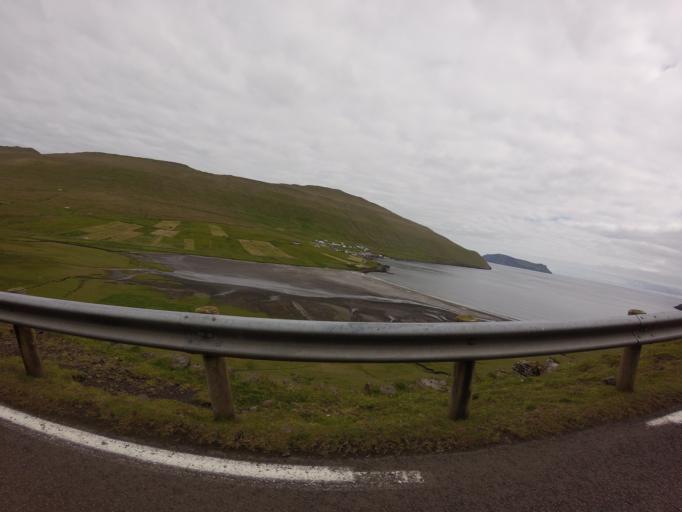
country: FO
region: Suduroy
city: Tvoroyri
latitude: 61.6241
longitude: -6.9353
